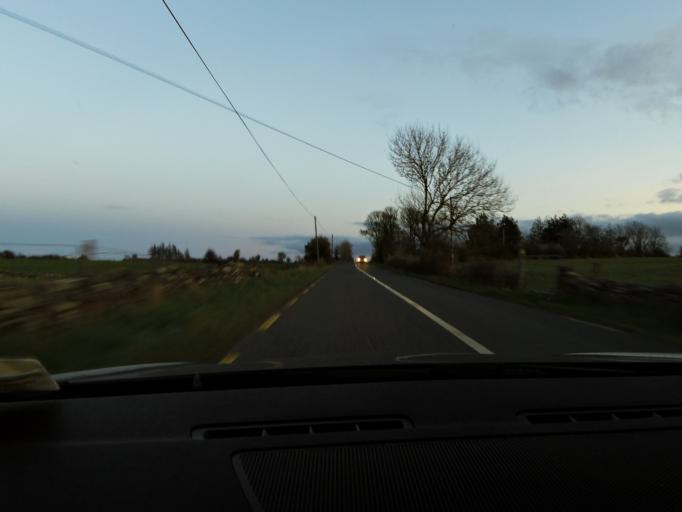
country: IE
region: Connaught
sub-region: Roscommon
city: Boyle
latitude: 53.8600
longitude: -8.2339
